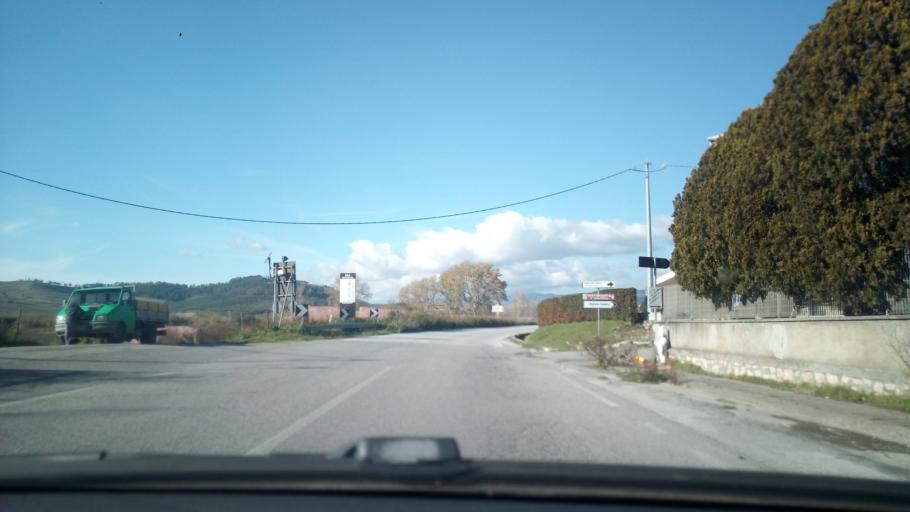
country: IT
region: Calabria
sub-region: Provincia di Catanzaro
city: Catanzaro
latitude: 38.8600
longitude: 16.5688
